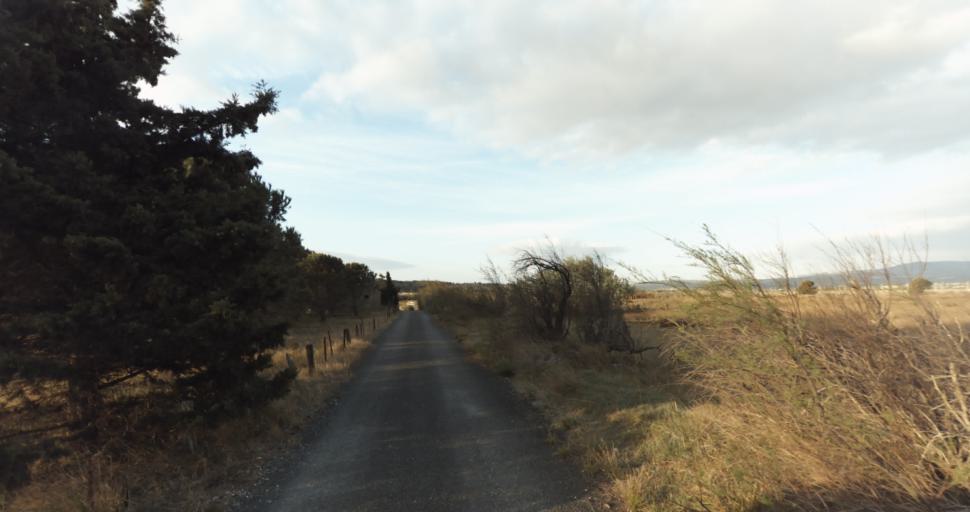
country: FR
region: Languedoc-Roussillon
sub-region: Departement de l'Aude
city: Leucate
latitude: 42.9436
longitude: 3.0282
